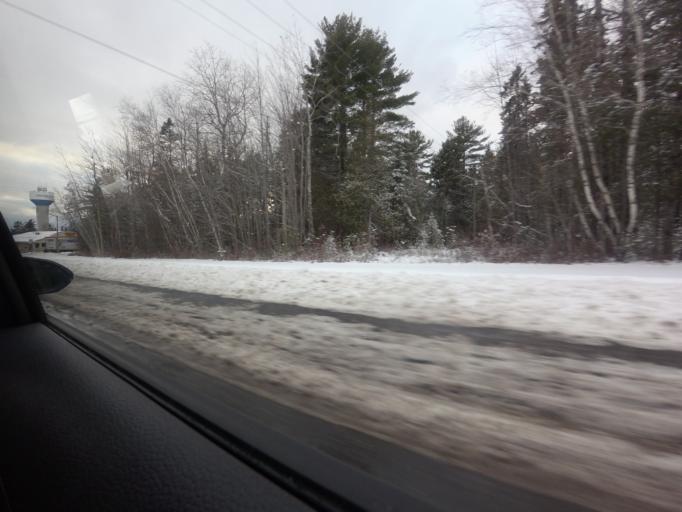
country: CA
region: New Brunswick
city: Oromocto
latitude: 45.8405
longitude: -66.4929
